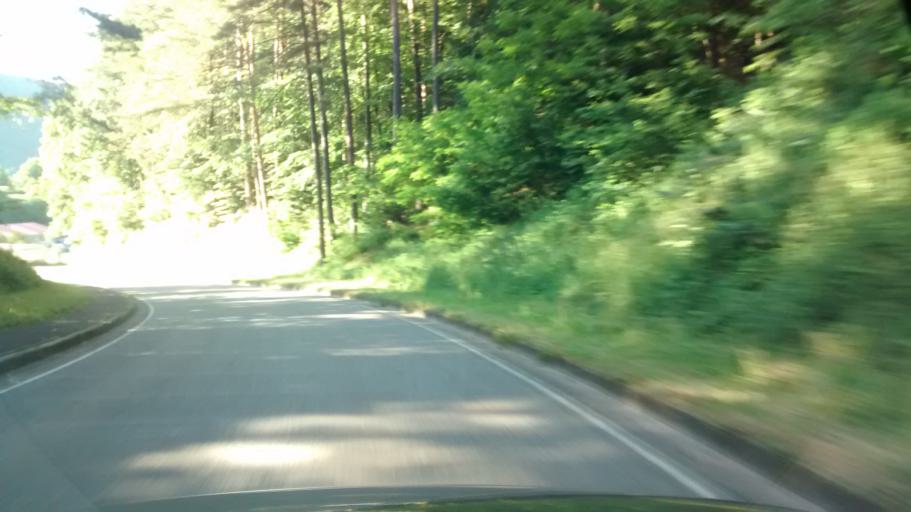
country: DE
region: Rheinland-Pfalz
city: Schindhard
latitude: 49.1372
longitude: 7.8234
